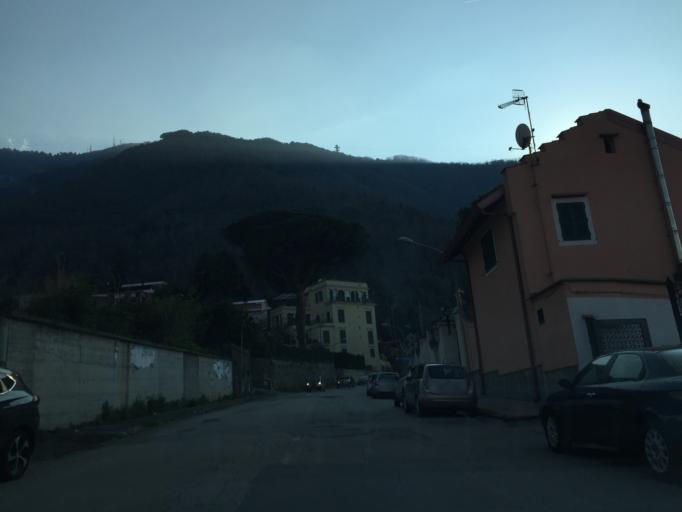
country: IT
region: Campania
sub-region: Provincia di Napoli
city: Castellammare di Stabia
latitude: 40.6877
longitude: 14.4861
